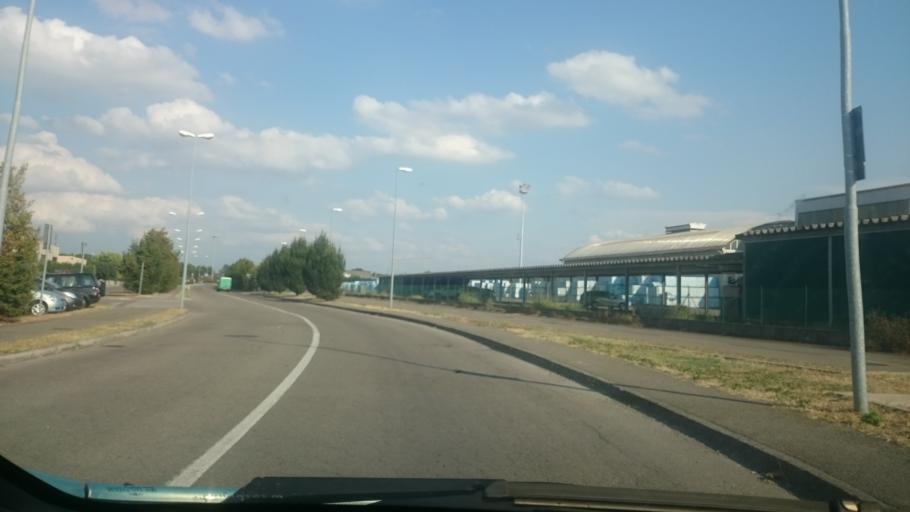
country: IT
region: Emilia-Romagna
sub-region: Provincia di Reggio Emilia
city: Rubiera
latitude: 44.6412
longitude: 10.7720
